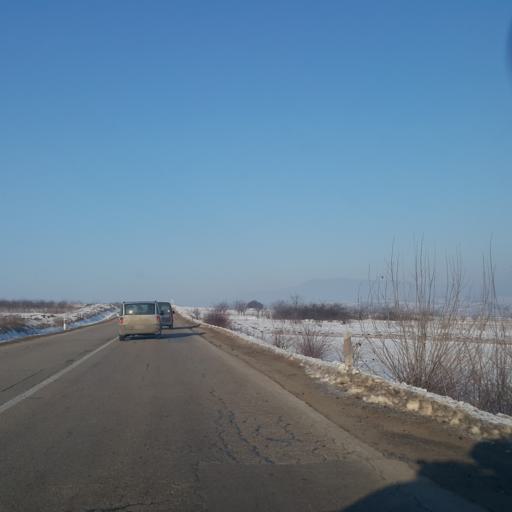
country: RS
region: Central Serbia
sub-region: Nisavski Okrug
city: Merosina
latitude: 43.2756
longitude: 21.6956
